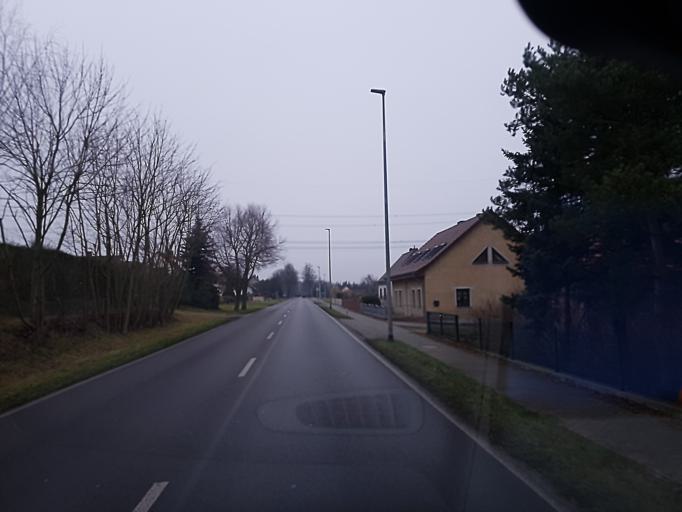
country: DE
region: Brandenburg
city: Lubbenau
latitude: 51.8819
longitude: 13.9058
